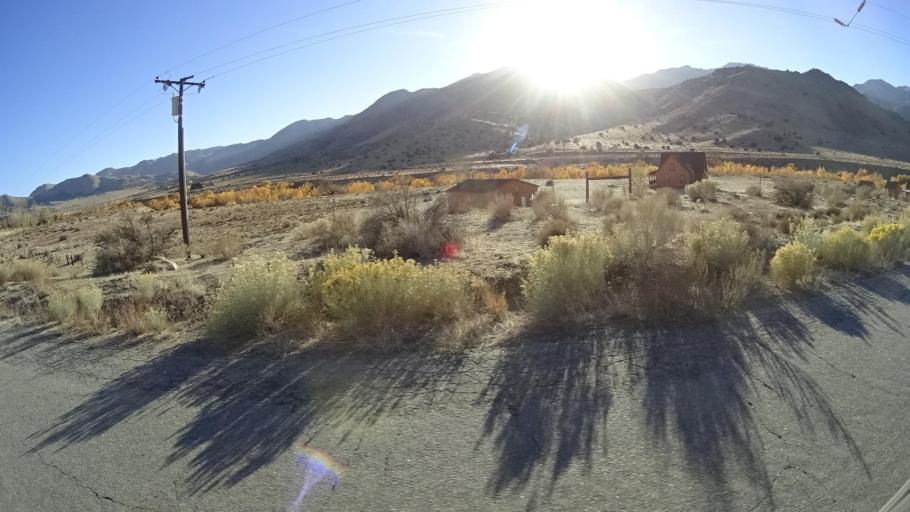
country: US
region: California
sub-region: Kern County
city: Weldon
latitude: 35.5695
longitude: -118.2471
